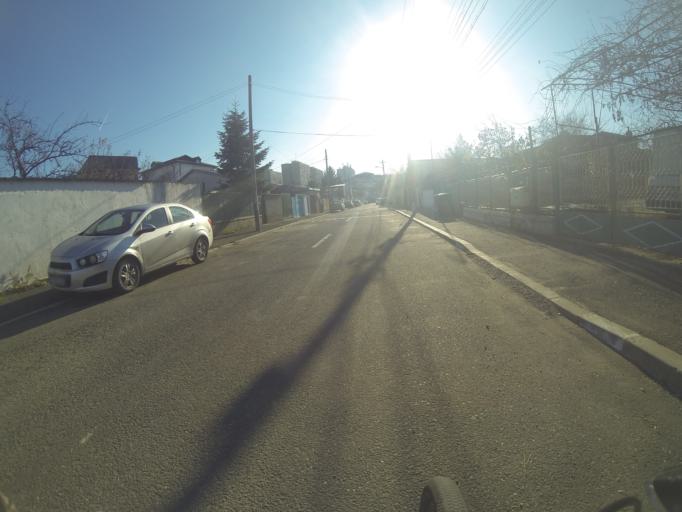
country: RO
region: Bucuresti
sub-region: Municipiul Bucuresti
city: Bucuresti
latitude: 44.3983
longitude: 26.0688
